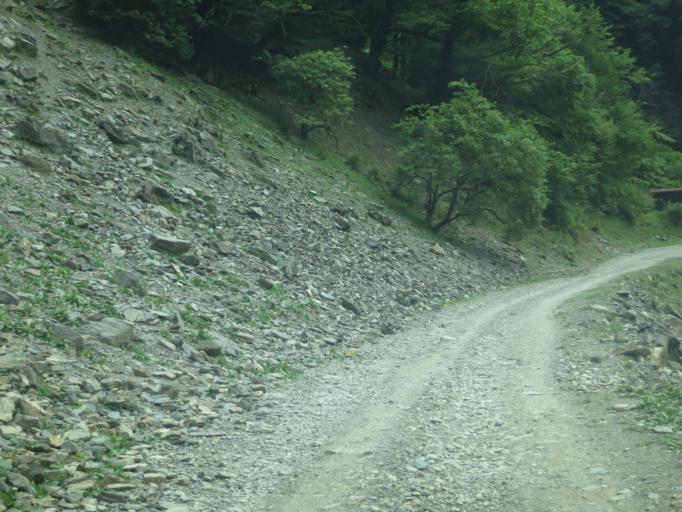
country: GE
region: Kakheti
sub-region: Telavi
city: Telavi
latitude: 42.2046
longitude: 45.4636
